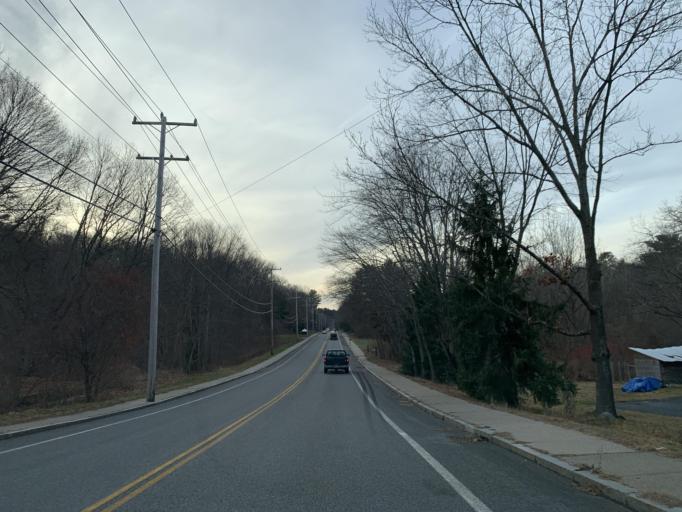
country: US
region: Rhode Island
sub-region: Providence County
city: Greenville
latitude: 41.8614
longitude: -71.5335
